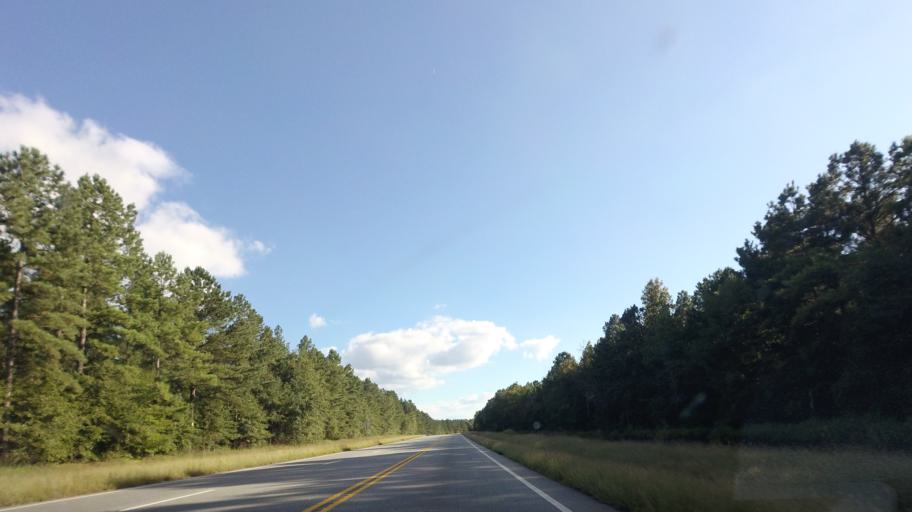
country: US
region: Georgia
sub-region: Lamar County
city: Barnesville
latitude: 32.9857
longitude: -84.2018
